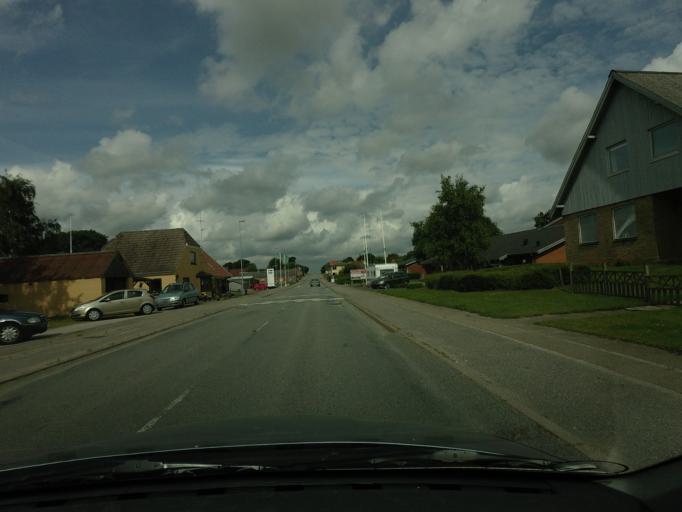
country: DK
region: North Denmark
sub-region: Hjorring Kommune
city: Tars
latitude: 57.3651
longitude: 10.1901
